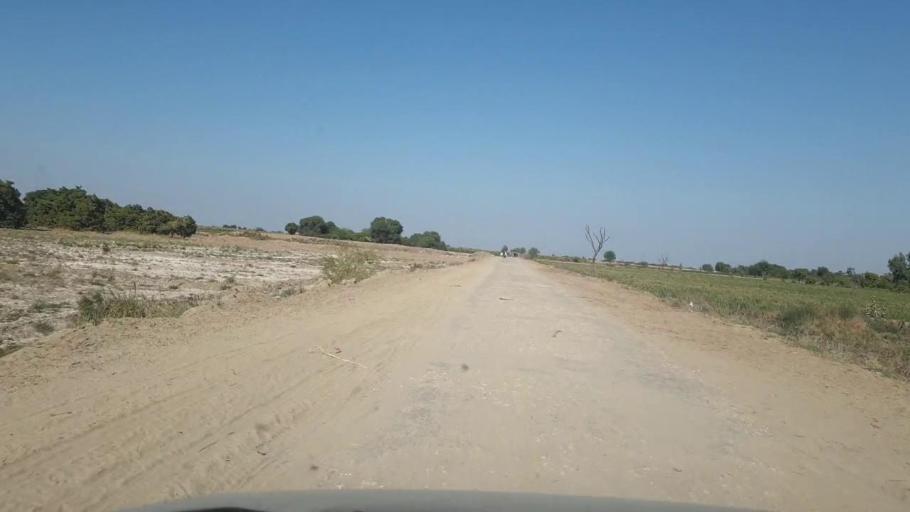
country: PK
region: Sindh
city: Samaro
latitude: 25.3380
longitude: 69.3110
